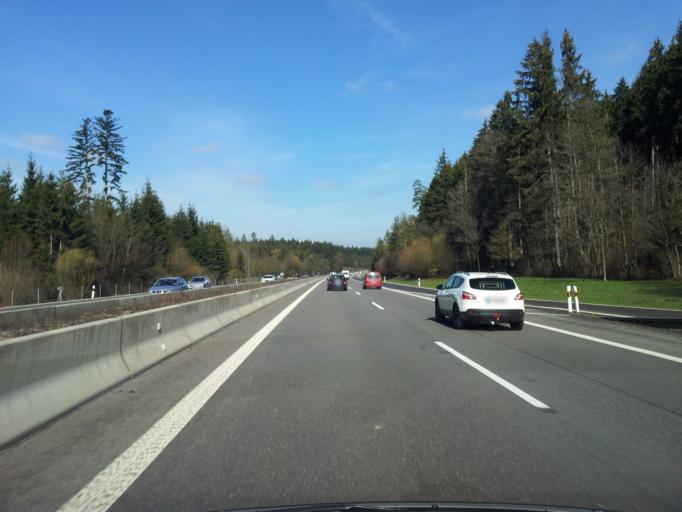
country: DE
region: Baden-Wuerttemberg
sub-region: Freiburg Region
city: Tuningen
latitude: 48.0709
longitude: 8.6058
